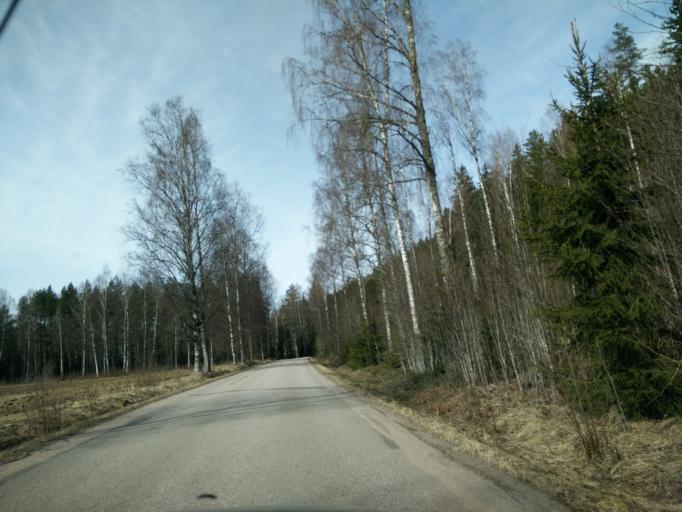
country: SE
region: Vaermland
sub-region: Hagfors Kommun
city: Hagfors
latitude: 60.0398
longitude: 13.5988
